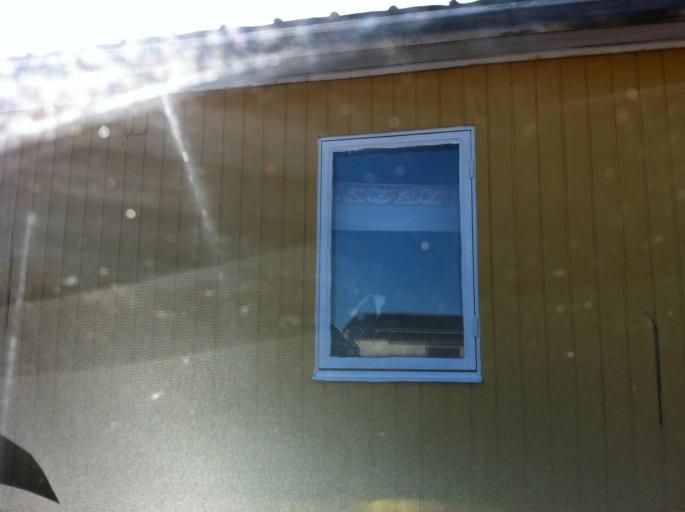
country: SE
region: Kalmar
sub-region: Borgholms Kommun
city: Borgholm
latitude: 57.2030
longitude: 16.9787
